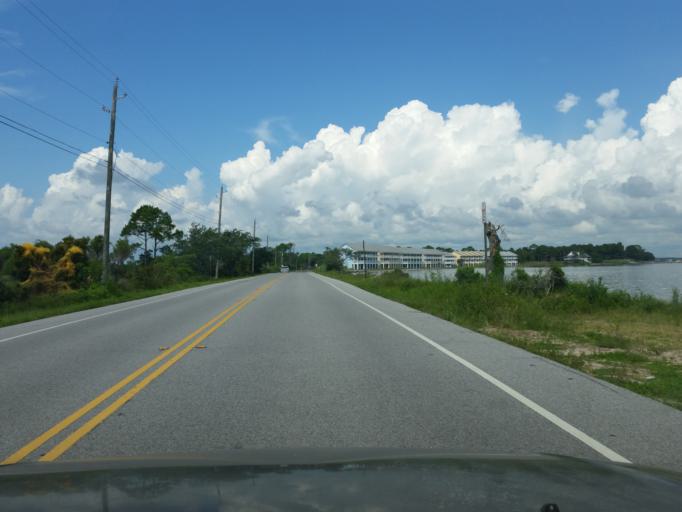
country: US
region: Alabama
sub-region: Baldwin County
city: Orange Beach
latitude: 30.3143
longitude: -87.4701
